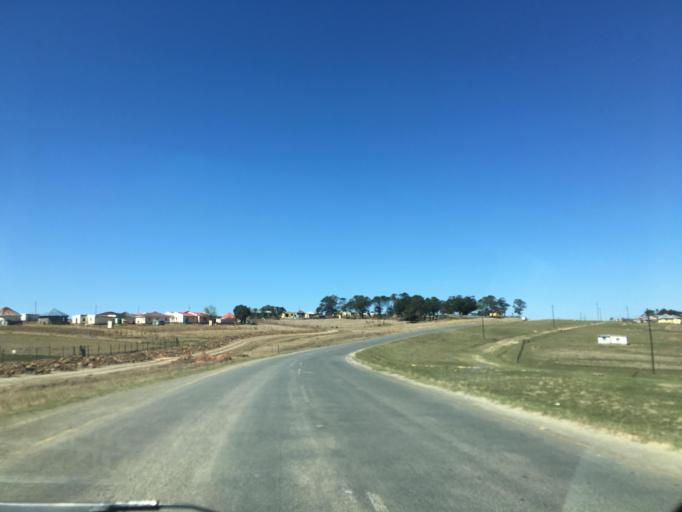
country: ZA
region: Eastern Cape
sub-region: Chris Hani District Municipality
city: Cala
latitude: -31.5513
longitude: 27.8929
